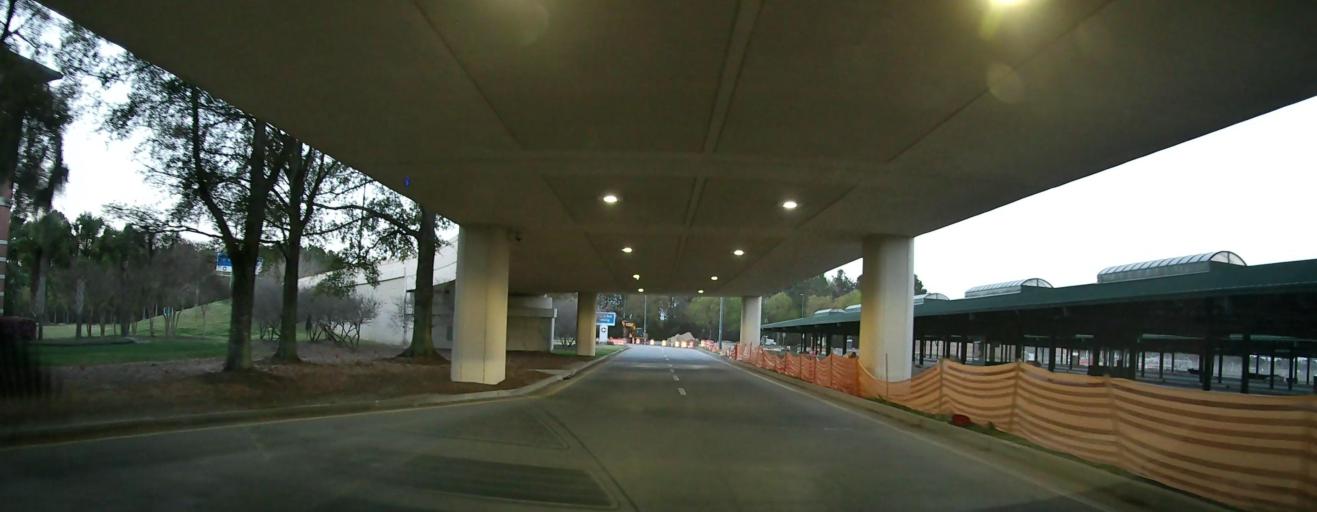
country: US
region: Georgia
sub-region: Chatham County
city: Pooler
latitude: 32.1372
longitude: -81.2103
